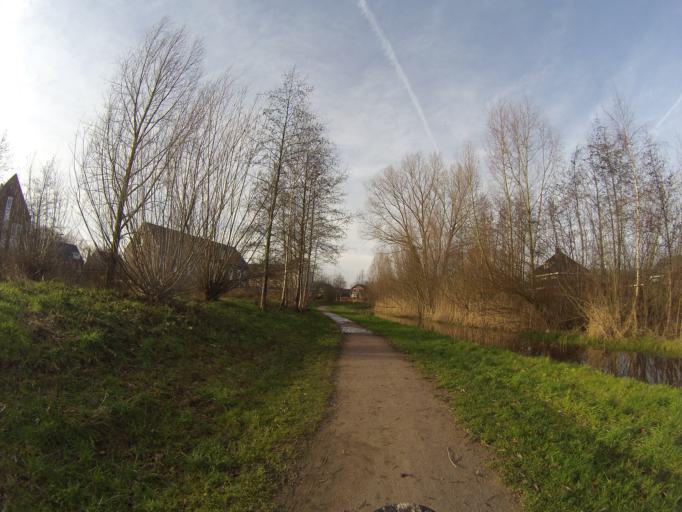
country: NL
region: Gelderland
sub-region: Gemeente Barneveld
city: Voorthuizen
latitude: 52.1919
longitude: 5.6096
